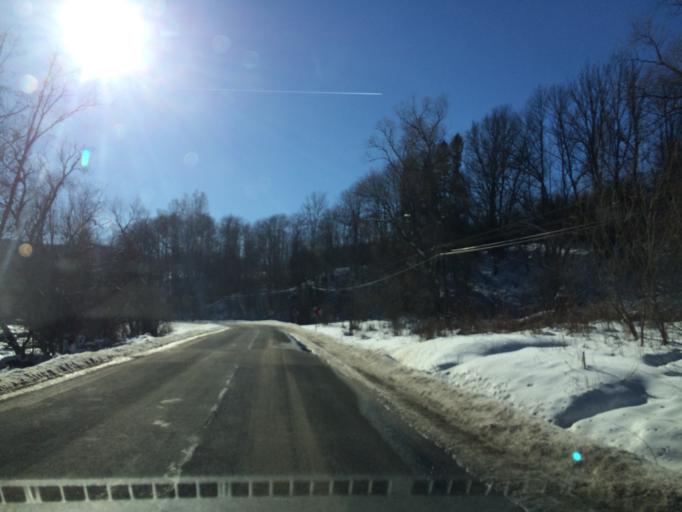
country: PL
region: Subcarpathian Voivodeship
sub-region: Powiat bieszczadzki
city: Lutowiska
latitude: 49.1731
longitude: 22.6864
